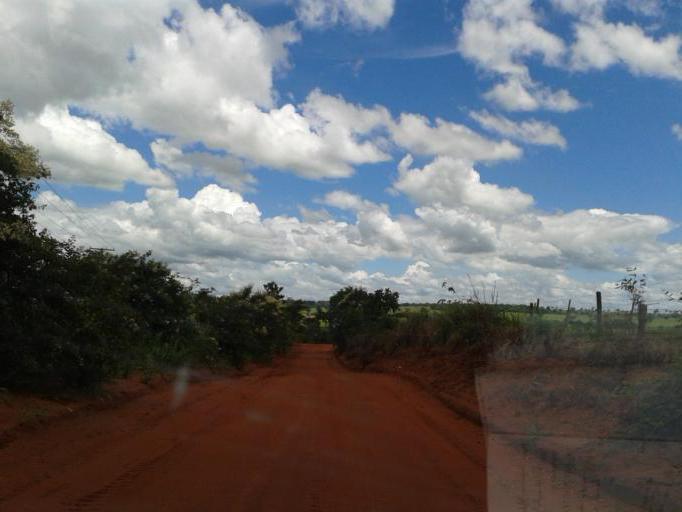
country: BR
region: Minas Gerais
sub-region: Santa Vitoria
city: Santa Vitoria
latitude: -18.8397
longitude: -50.1062
